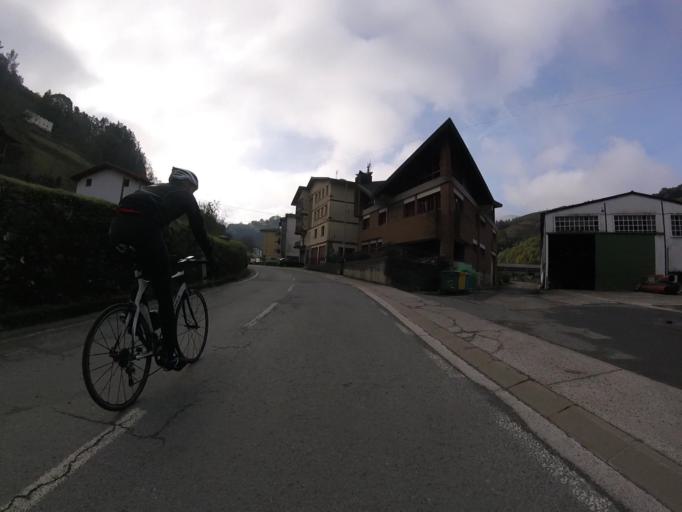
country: ES
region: Navarre
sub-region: Provincia de Navarra
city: Goizueta
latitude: 43.1748
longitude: -1.8631
